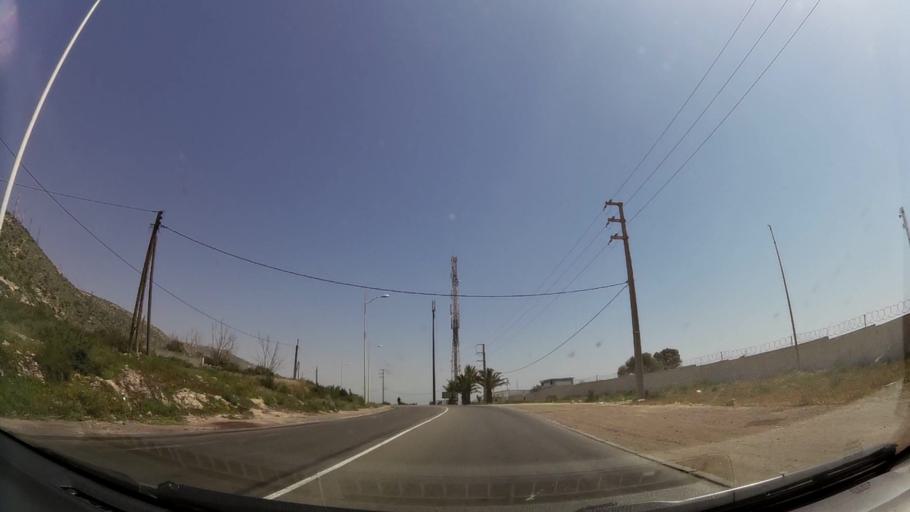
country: MA
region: Souss-Massa-Draa
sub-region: Agadir-Ida-ou-Tnan
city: Agadir
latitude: 30.4344
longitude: -9.6430
